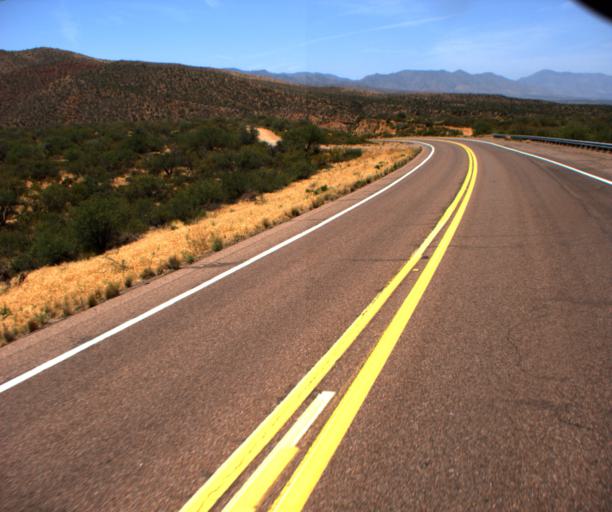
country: US
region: Arizona
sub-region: Gila County
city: Tonto Basin
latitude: 33.7250
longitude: -111.2063
